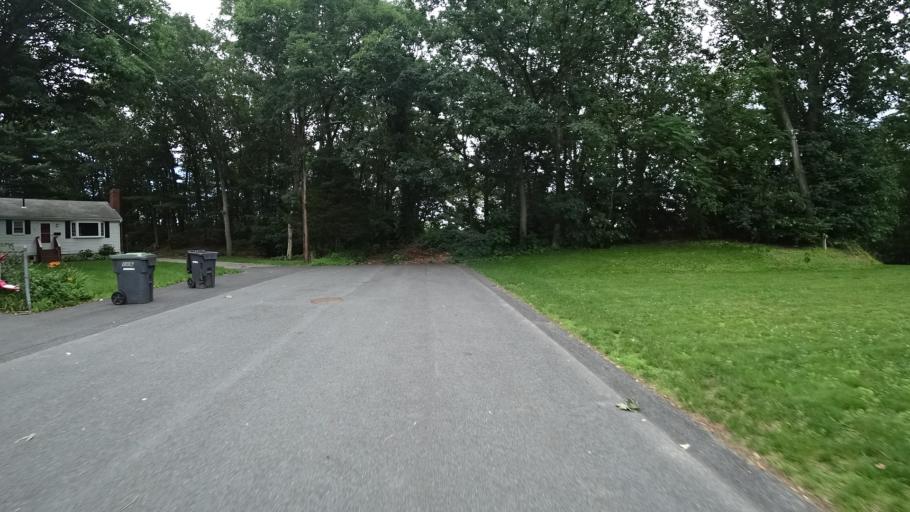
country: US
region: Massachusetts
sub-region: Norfolk County
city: Dedham
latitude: 42.2343
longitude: -71.1453
